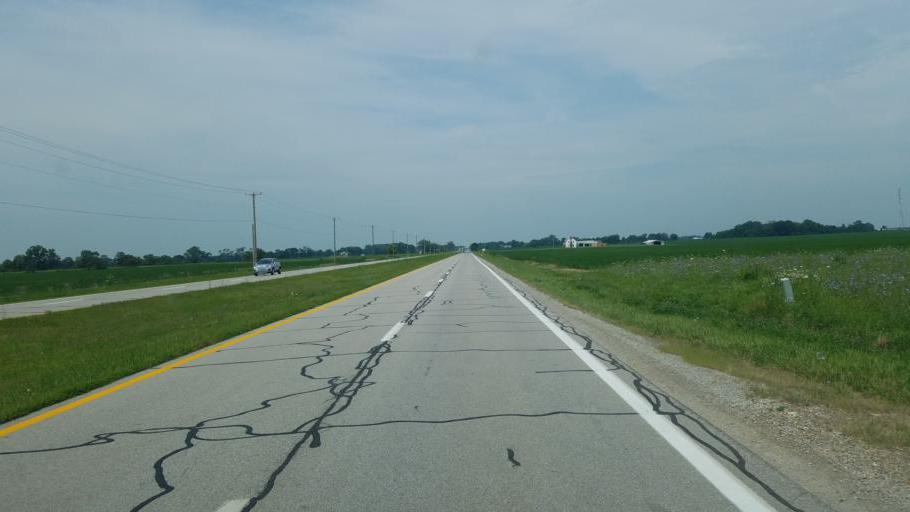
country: US
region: Ohio
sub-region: Madison County
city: London
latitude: 39.9395
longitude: -83.3709
